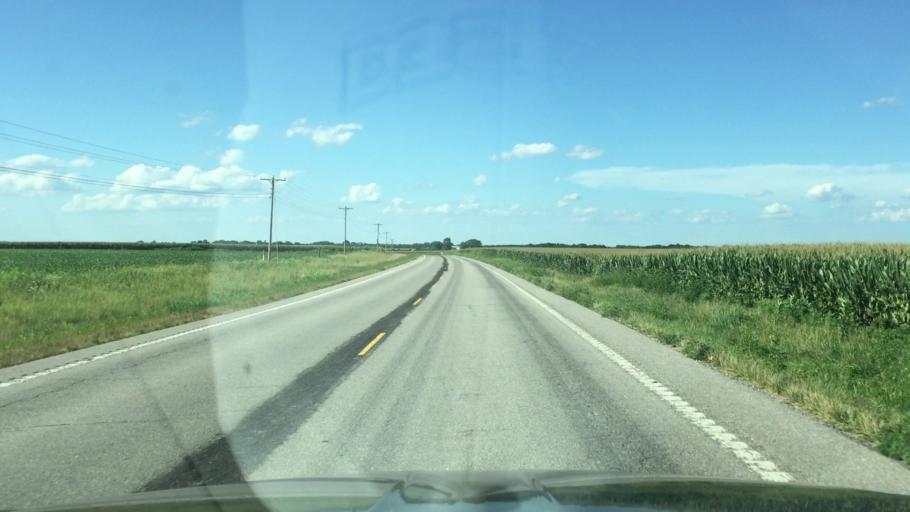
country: US
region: Missouri
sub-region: Moniteau County
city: Tipton
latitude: 38.5793
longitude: -92.7916
